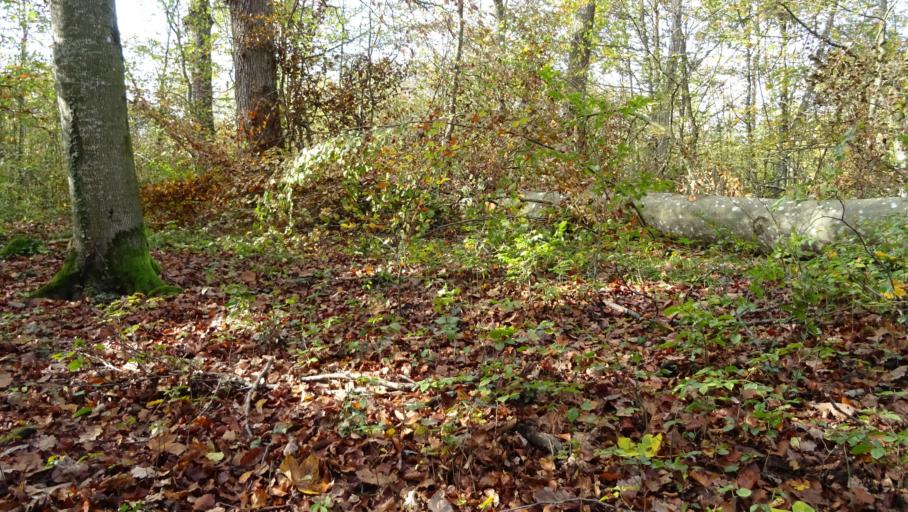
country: DE
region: Baden-Wuerttemberg
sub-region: Karlsruhe Region
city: Binau
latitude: 49.3725
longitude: 9.0479
